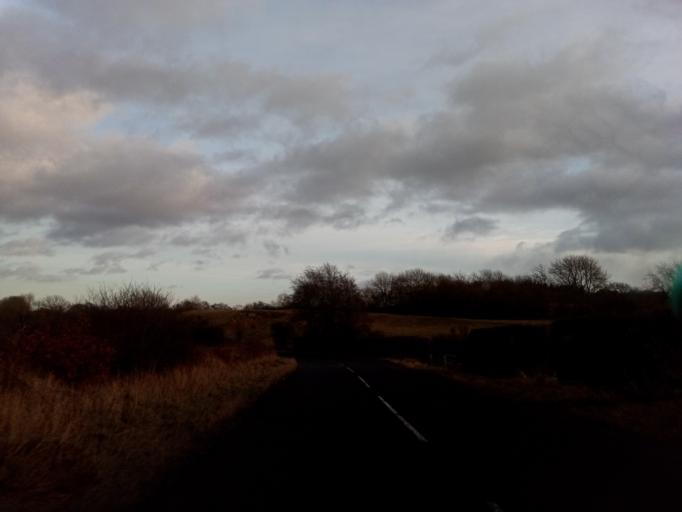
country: GB
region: Scotland
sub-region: The Scottish Borders
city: Melrose
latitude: 55.5539
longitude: -2.7388
